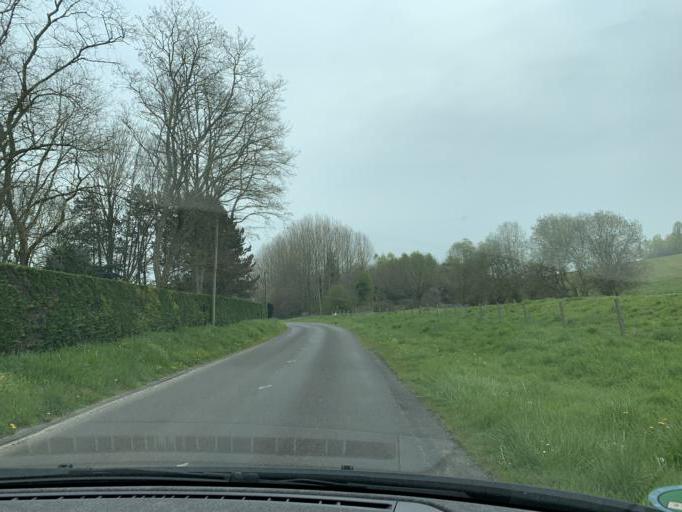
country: FR
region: Haute-Normandie
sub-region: Departement de la Seine-Maritime
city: Saint-Valery-en-Caux
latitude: 49.8548
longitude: 0.7254
